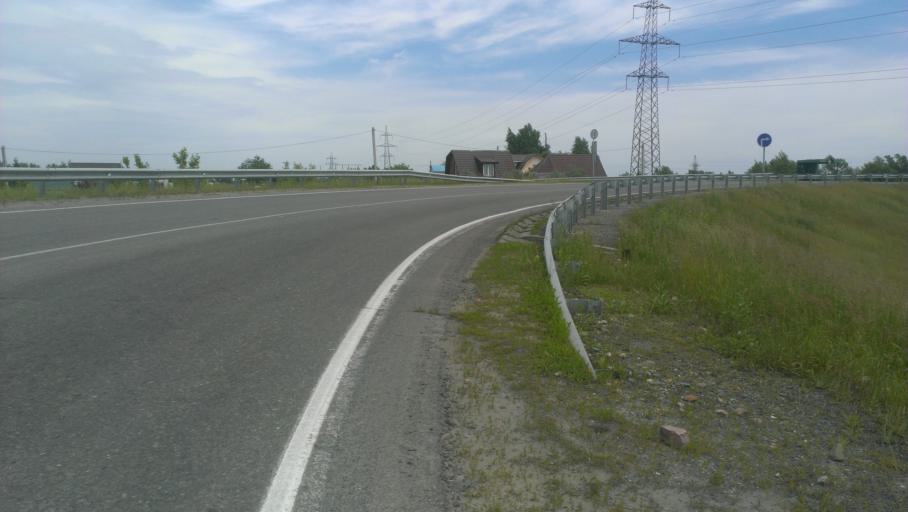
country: RU
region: Altai Krai
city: Sannikovo
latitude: 53.3412
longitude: 83.9343
